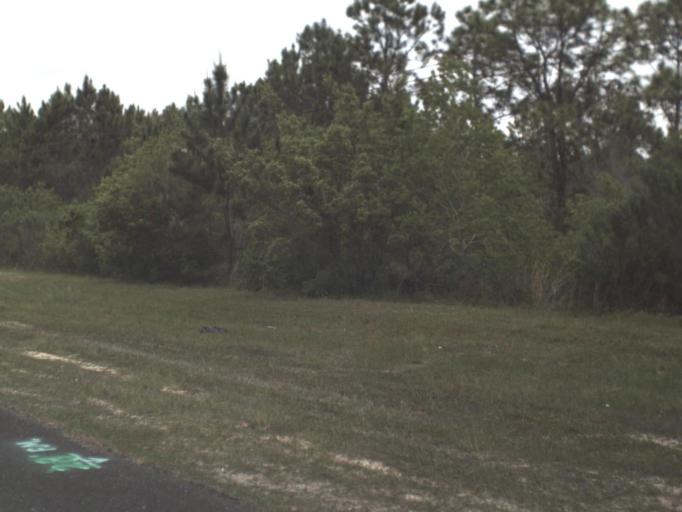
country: US
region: Florida
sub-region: Santa Rosa County
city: Bagdad
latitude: 30.5010
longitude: -87.0809
